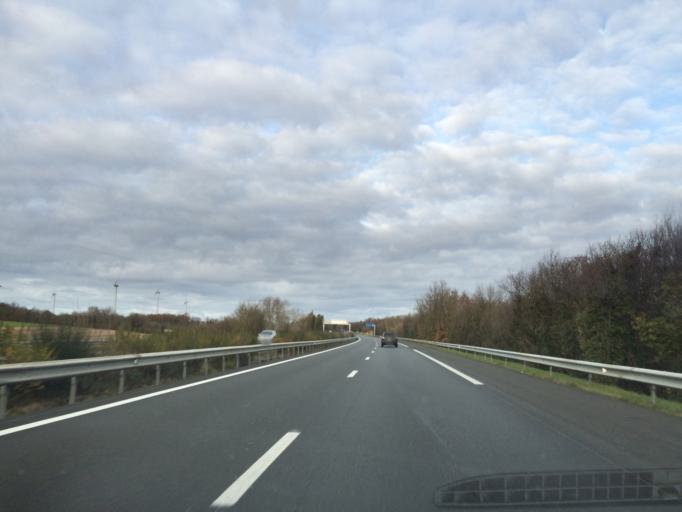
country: FR
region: Poitou-Charentes
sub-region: Departement de la Charente-Maritime
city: Saint-Jean-d'Angely
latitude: 46.0033
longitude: -0.5414
